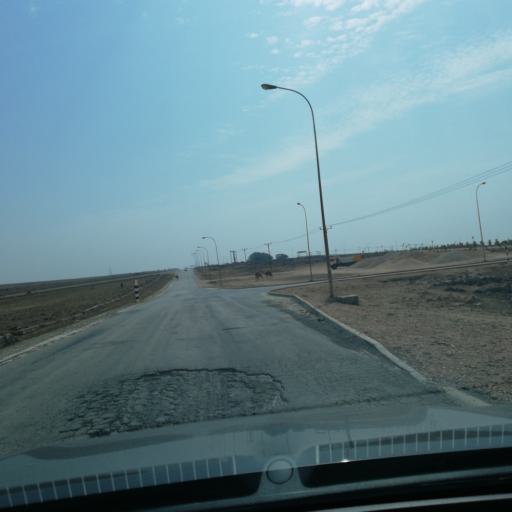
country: OM
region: Zufar
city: Salalah
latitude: 17.2426
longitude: 54.0663
